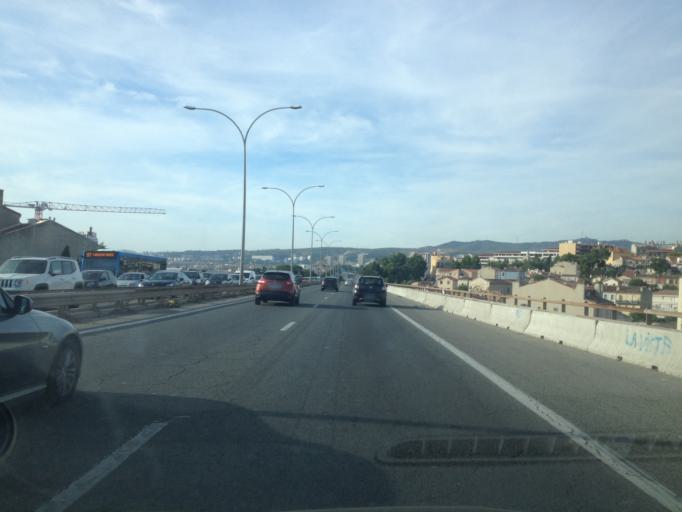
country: FR
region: Provence-Alpes-Cote d'Azur
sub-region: Departement des Bouches-du-Rhone
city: Marseille 03
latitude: 43.3115
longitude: 5.3763
